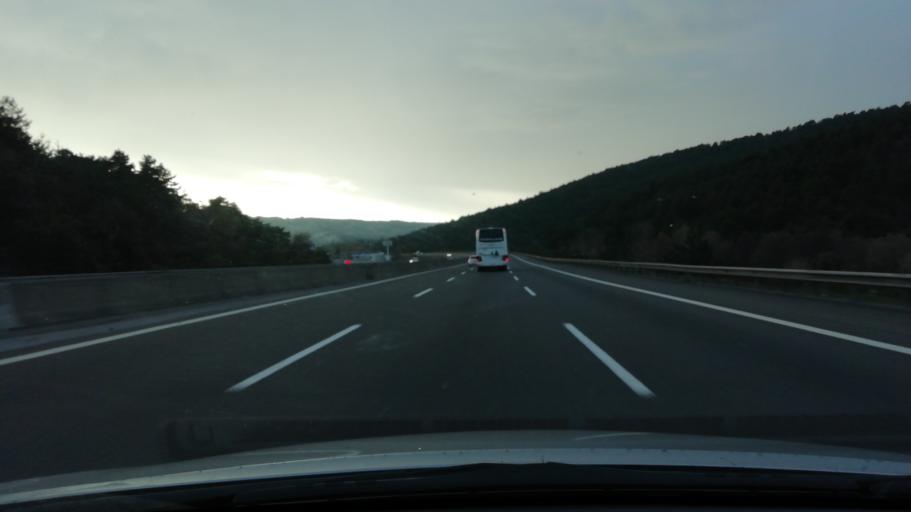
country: TR
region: Bolu
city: Gokcesu
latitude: 40.7394
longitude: 31.8314
